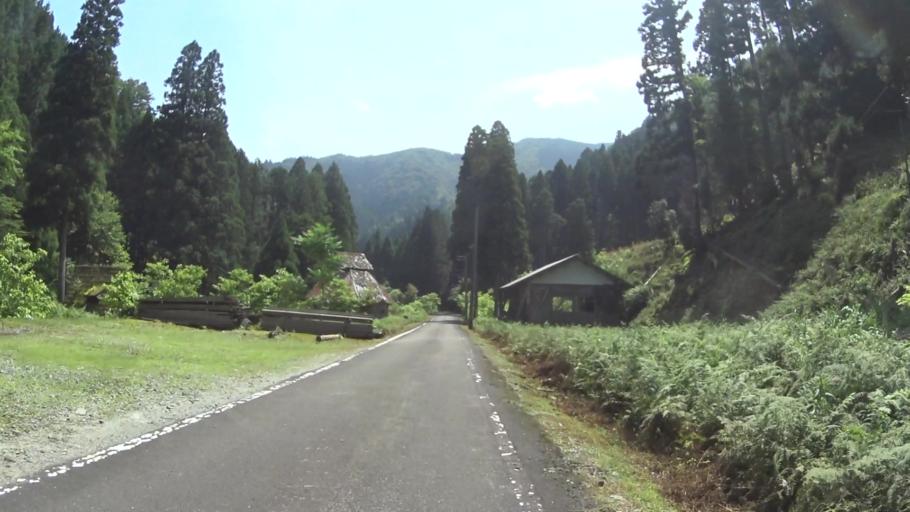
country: JP
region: Kyoto
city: Maizuru
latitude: 35.3459
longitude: 135.5241
